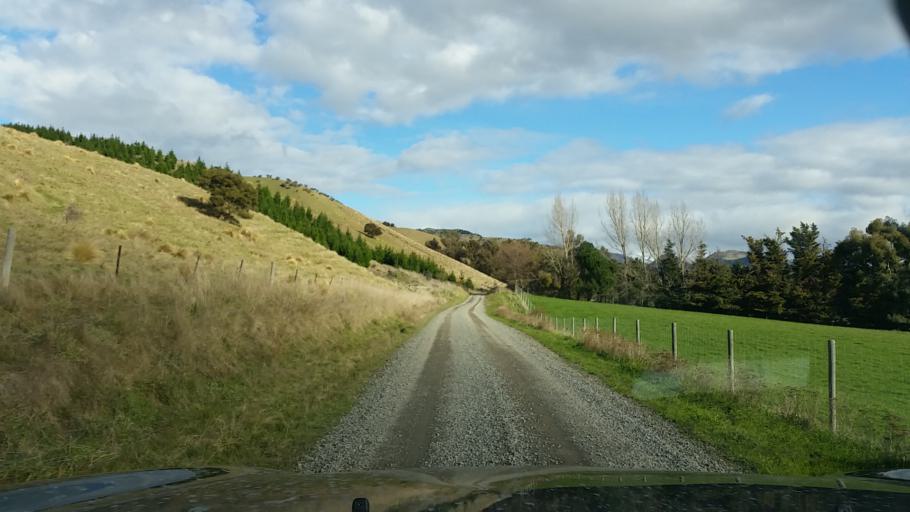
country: NZ
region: Marlborough
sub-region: Marlborough District
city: Blenheim
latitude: -41.7732
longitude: 173.8555
